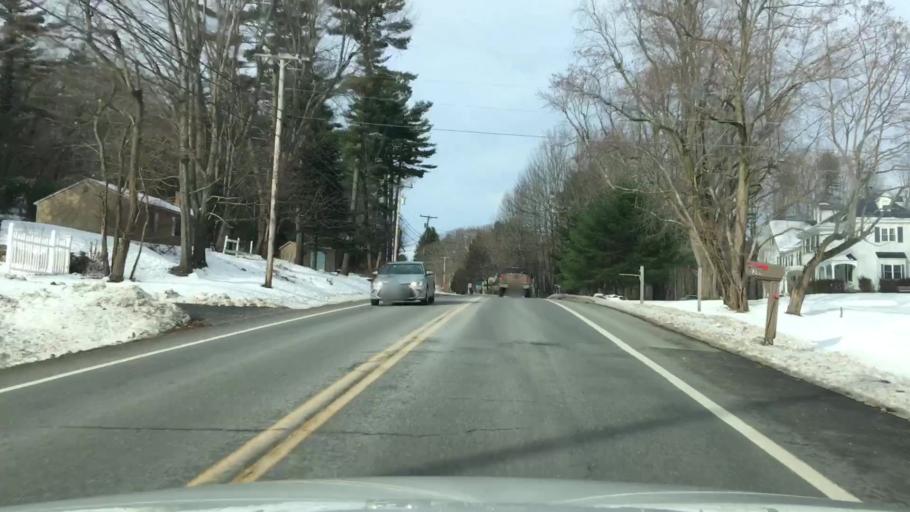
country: US
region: Maine
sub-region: Kennebec County
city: Winthrop
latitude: 44.3187
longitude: -69.9781
